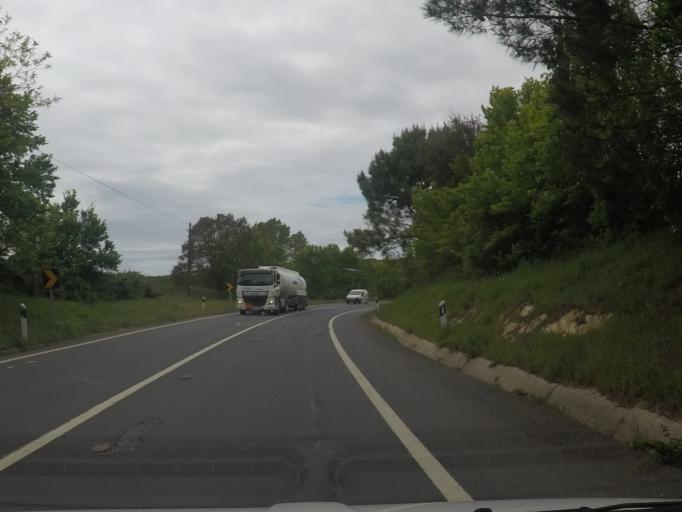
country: PT
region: Setubal
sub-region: Santiago do Cacem
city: Cercal
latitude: 37.8267
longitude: -8.6968
